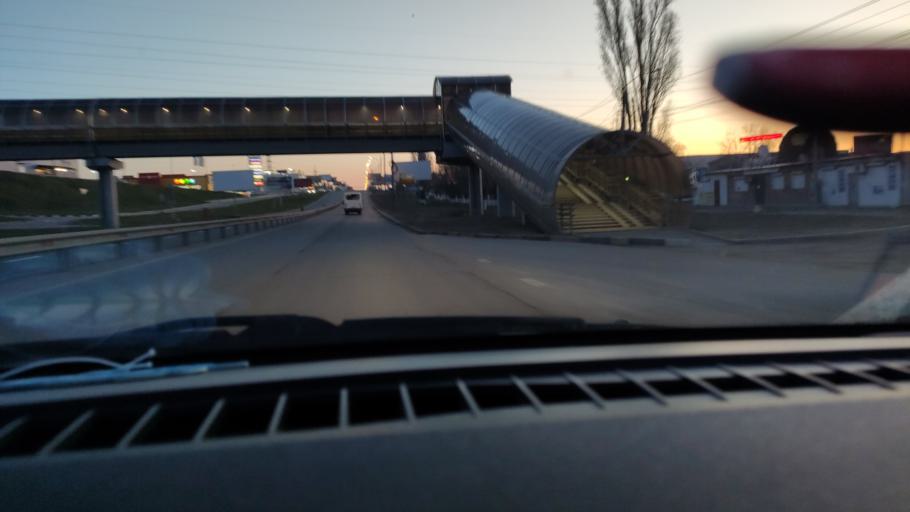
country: RU
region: Saratov
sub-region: Saratovskiy Rayon
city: Saratov
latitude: 51.6192
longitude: 45.9737
